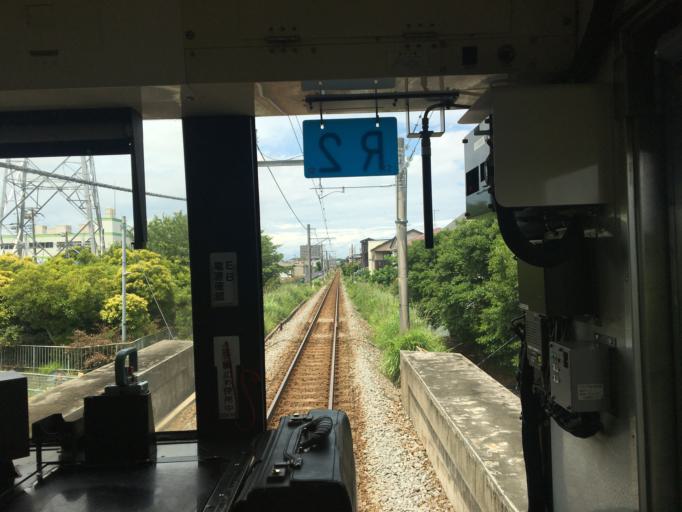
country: JP
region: Kanagawa
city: Chigasaki
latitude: 35.3417
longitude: 139.4063
